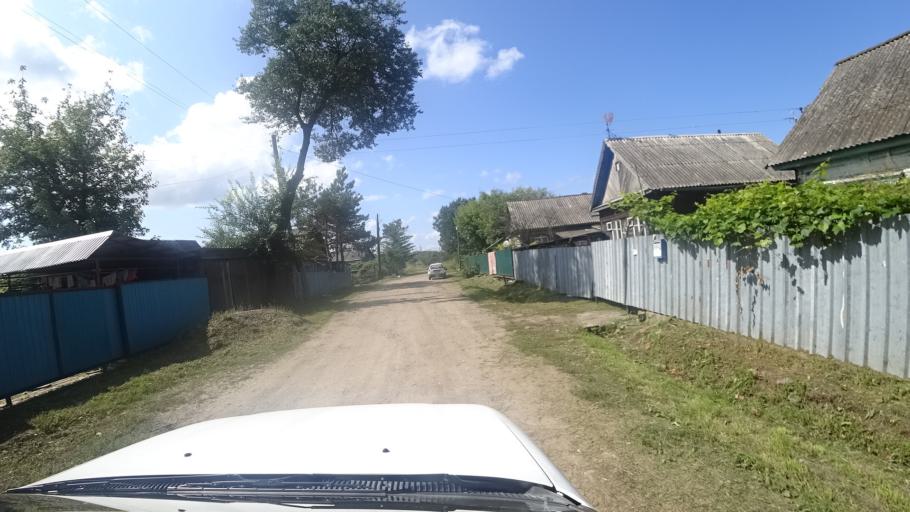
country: RU
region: Primorskiy
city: Dal'nerechensk
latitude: 45.9250
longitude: 133.7165
